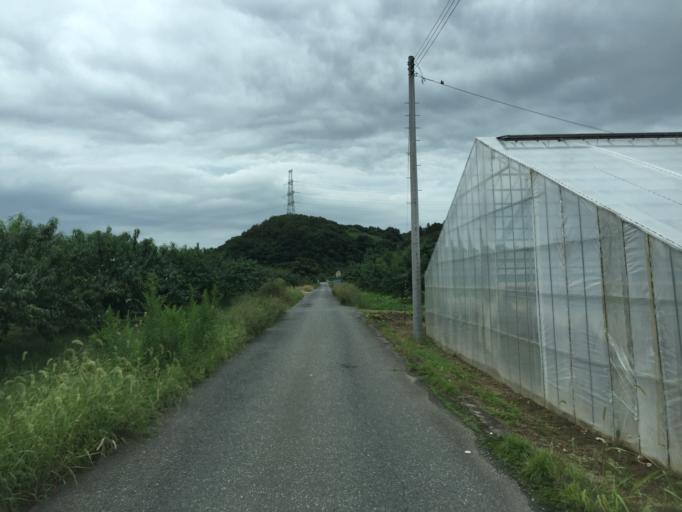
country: JP
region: Fukushima
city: Hobaramachi
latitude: 37.7986
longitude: 140.5088
